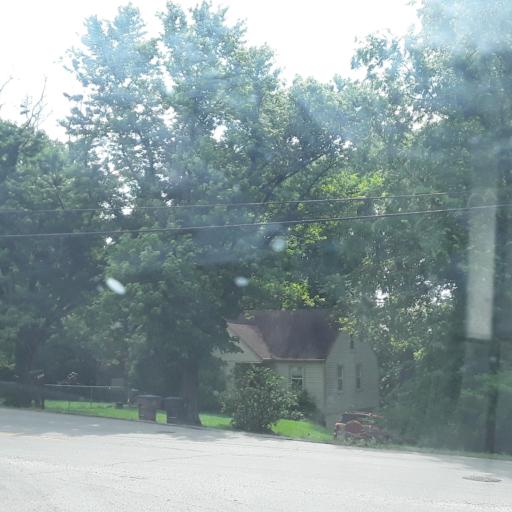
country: US
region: Tennessee
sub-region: Davidson County
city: Oak Hill
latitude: 36.1106
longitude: -86.7312
